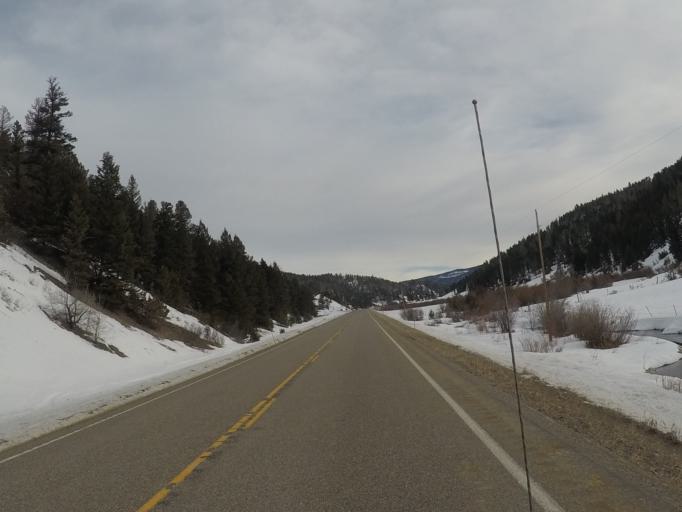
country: US
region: Montana
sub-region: Meagher County
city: White Sulphur Springs
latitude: 46.6816
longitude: -110.8757
